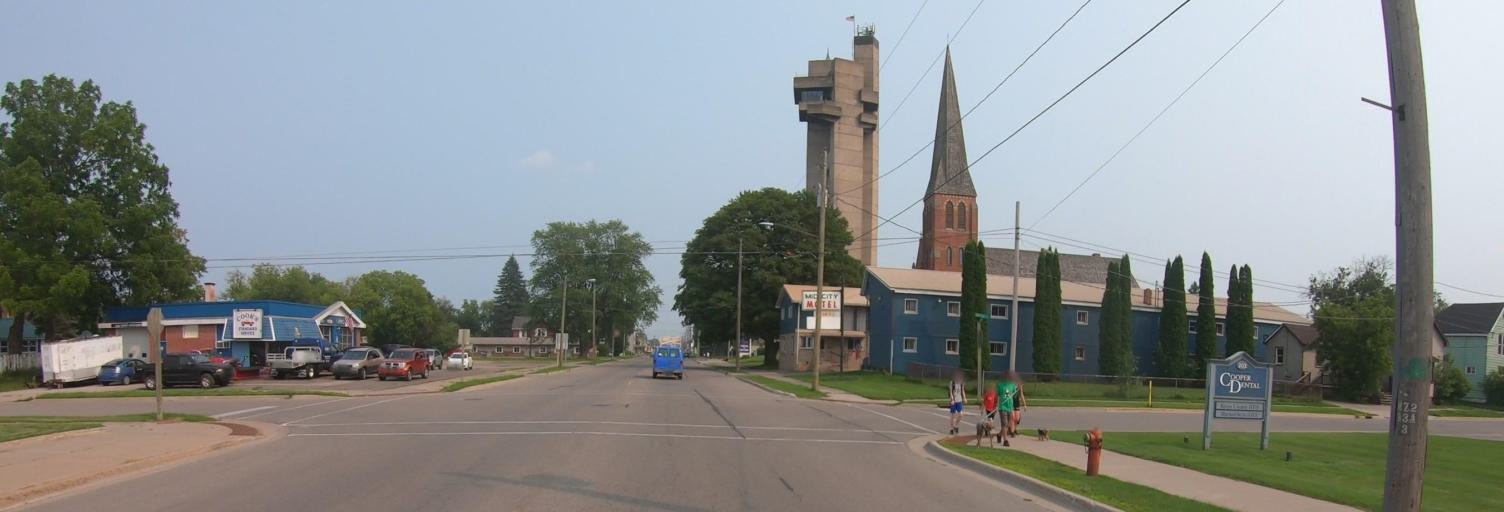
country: US
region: Michigan
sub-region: Chippewa County
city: Sault Ste. Marie
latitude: 46.4992
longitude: -84.3423
